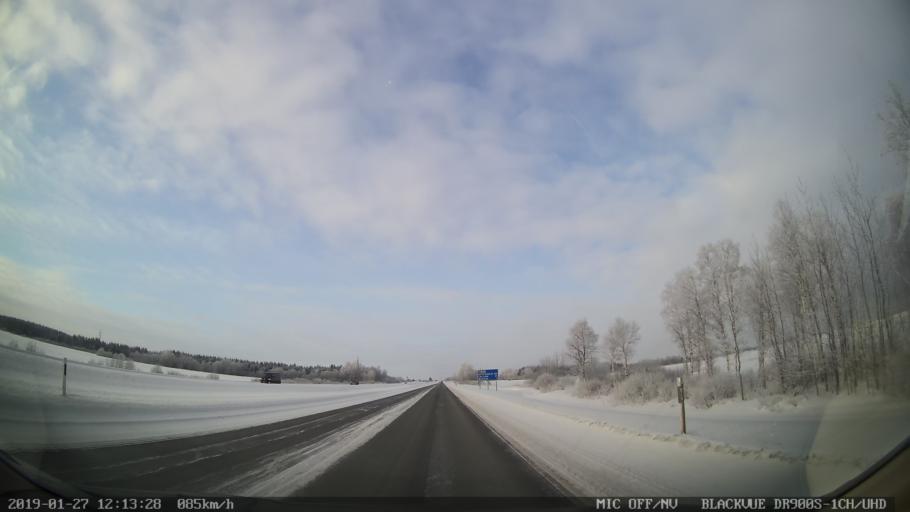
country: EE
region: Harju
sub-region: Raasiku vald
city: Raasiku
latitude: 59.4370
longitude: 25.1580
